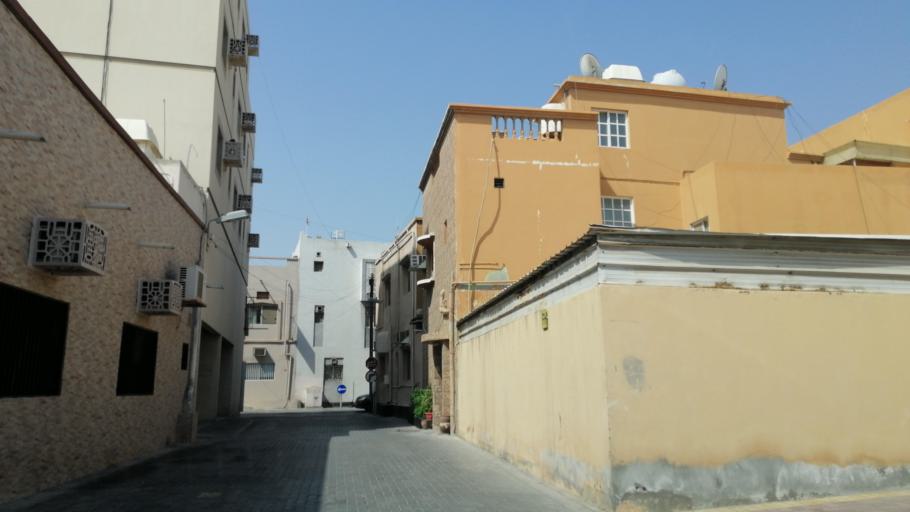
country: BH
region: Muharraq
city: Al Hadd
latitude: 26.2479
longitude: 50.6547
